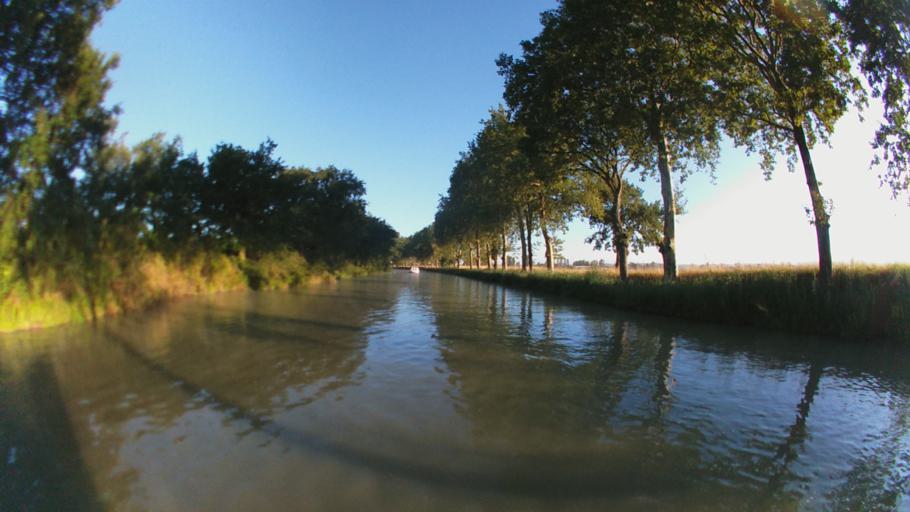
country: FR
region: Midi-Pyrenees
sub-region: Departement de la Haute-Garonne
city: Villenouvelle
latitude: 43.4100
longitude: 1.6627
